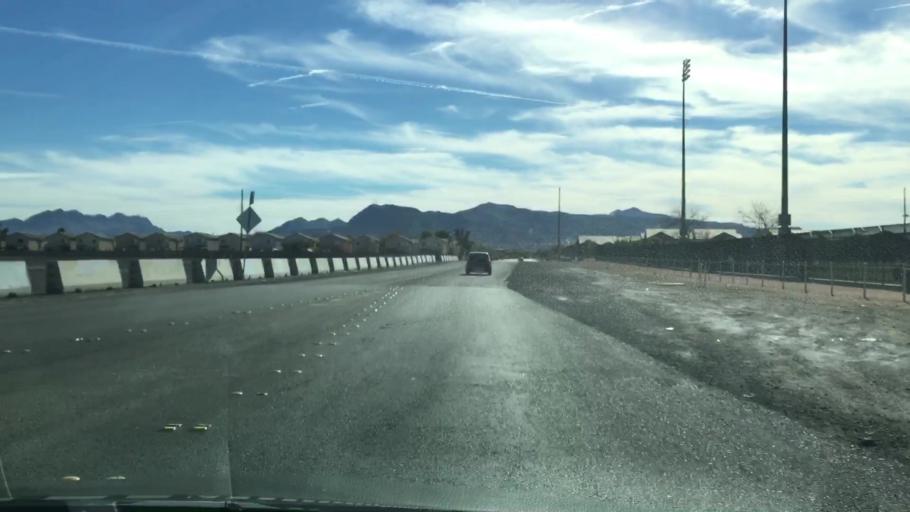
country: US
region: Nevada
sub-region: Clark County
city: Henderson
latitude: 36.0843
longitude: -115.0205
